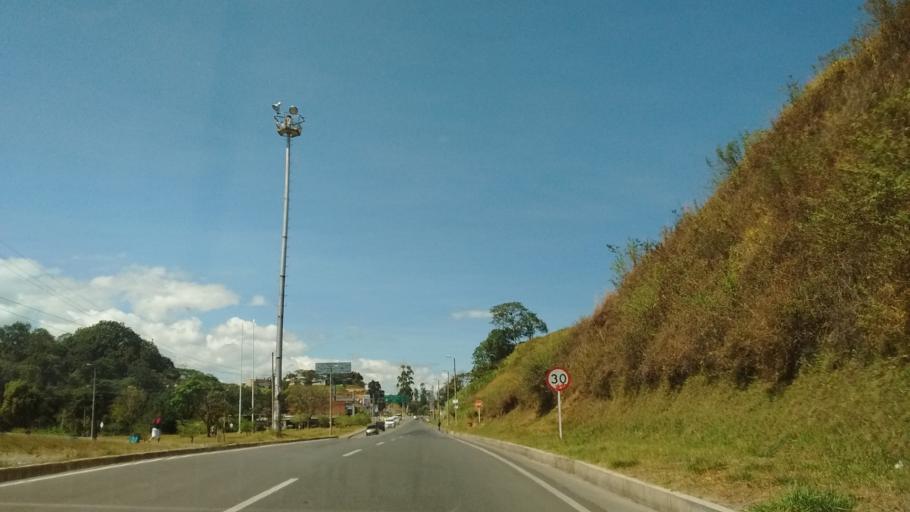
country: CO
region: Cauca
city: Popayan
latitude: 2.4314
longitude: -76.6206
